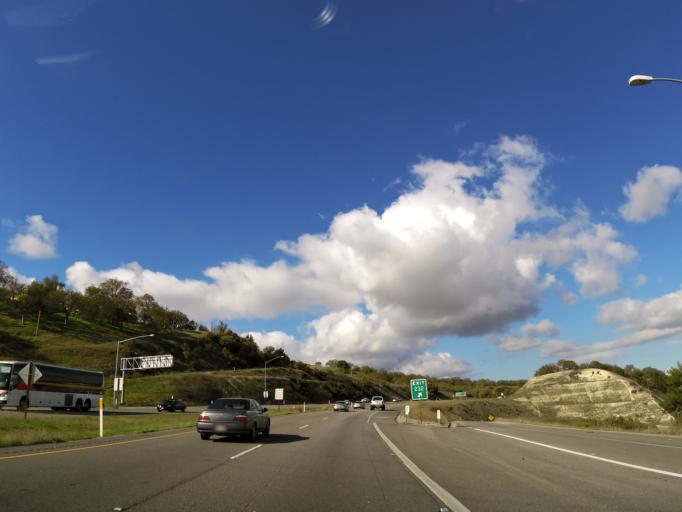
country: US
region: California
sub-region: San Luis Obispo County
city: Paso Robles
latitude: 35.6544
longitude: -120.6956
